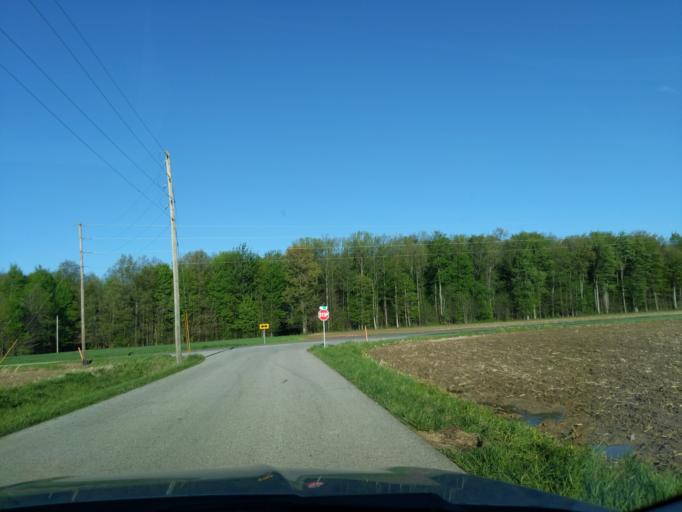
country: US
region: Indiana
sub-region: Decatur County
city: Westport
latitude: 39.1979
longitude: -85.5464
